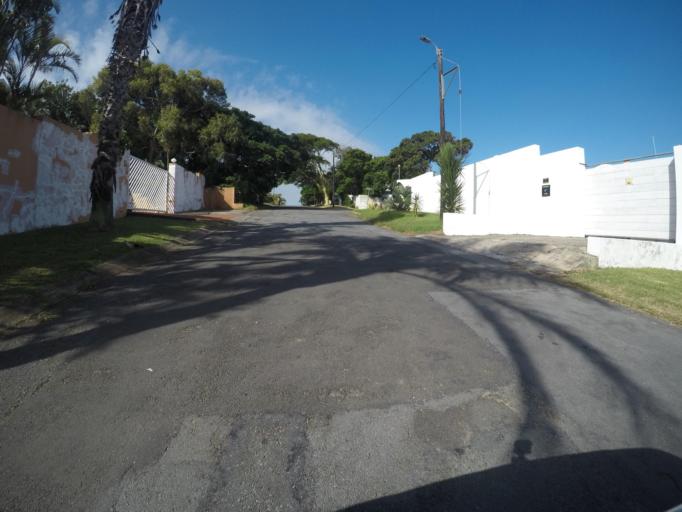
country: ZA
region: Eastern Cape
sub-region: Buffalo City Metropolitan Municipality
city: East London
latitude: -32.9756
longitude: 27.9553
